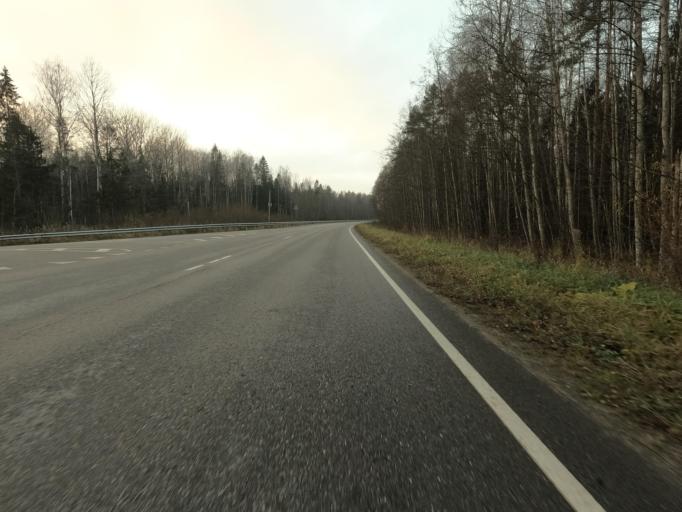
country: RU
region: Leningrad
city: Kirovsk
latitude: 59.8177
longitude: 30.9735
